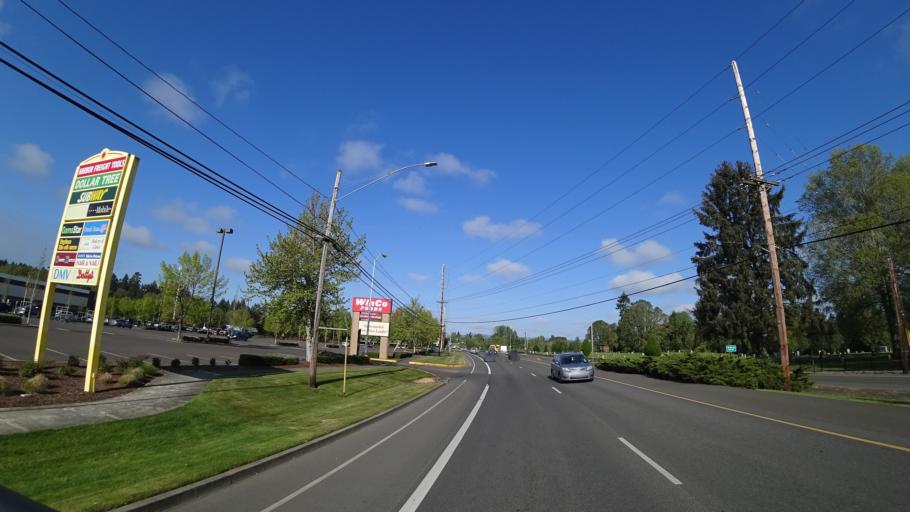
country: US
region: Oregon
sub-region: Washington County
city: Hillsboro
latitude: 45.5198
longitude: -123.0057
